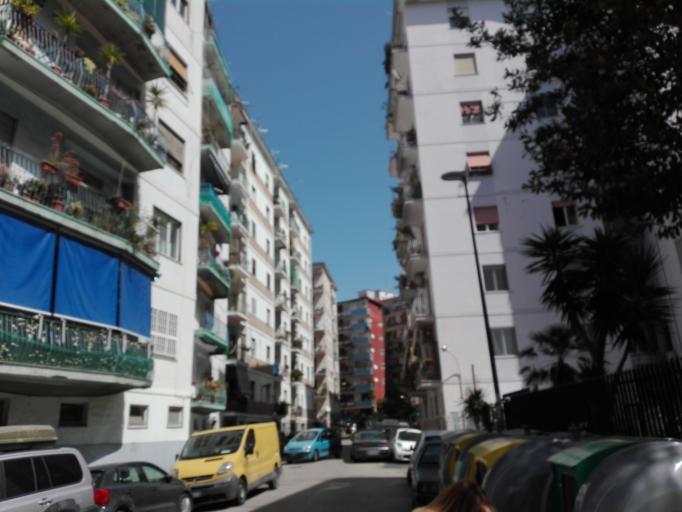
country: IT
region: Campania
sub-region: Provincia di Napoli
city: Napoli
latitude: 40.8509
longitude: 14.2231
